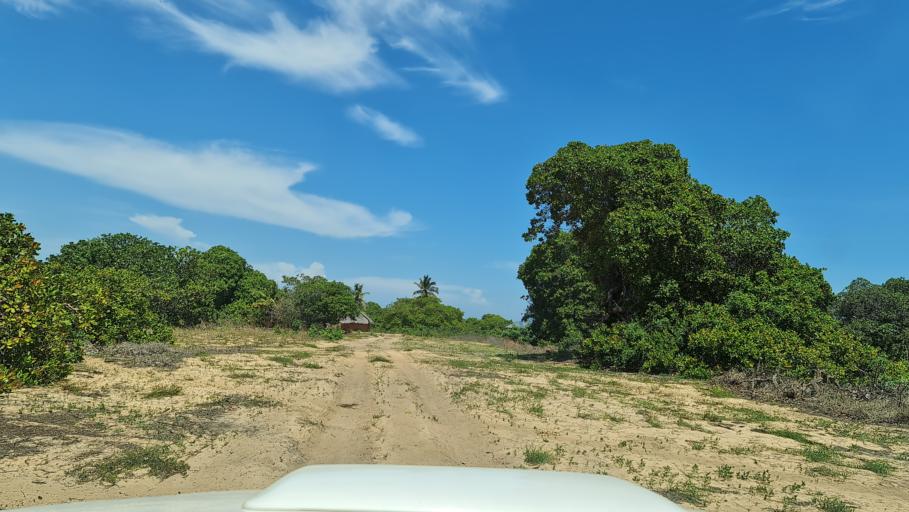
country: MZ
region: Nampula
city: Ilha de Mocambique
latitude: -15.1983
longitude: 40.6113
